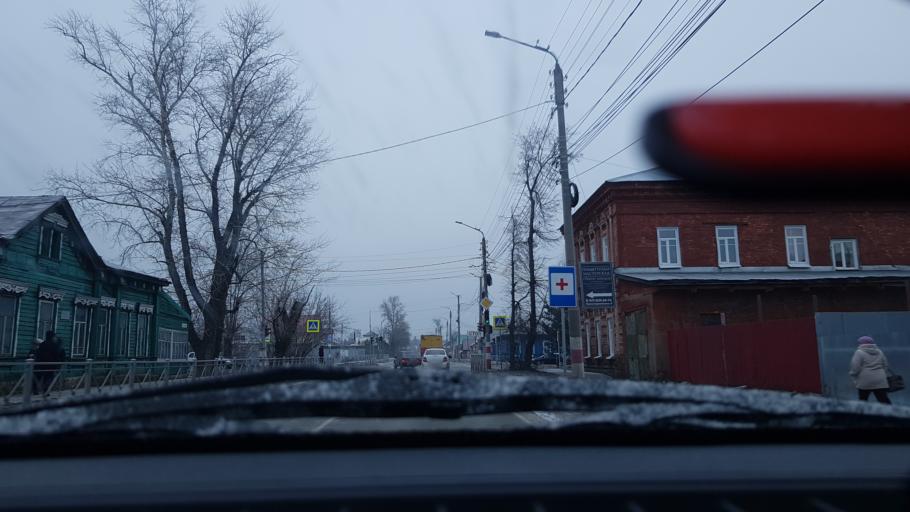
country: RU
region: Ulyanovsk
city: Dimitrovgrad
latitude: 54.2208
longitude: 49.6239
